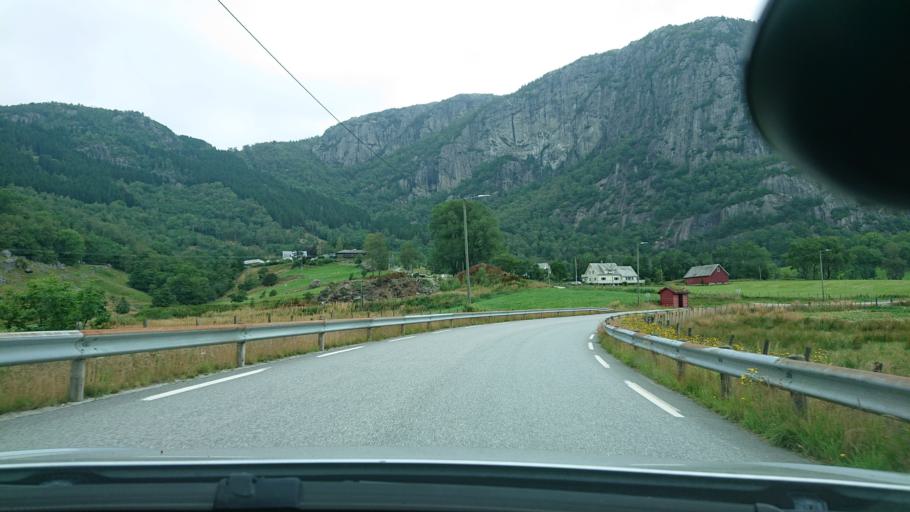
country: NO
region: Rogaland
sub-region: Hjelmeland
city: Hjelmelandsvagen
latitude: 59.2320
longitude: 6.1970
